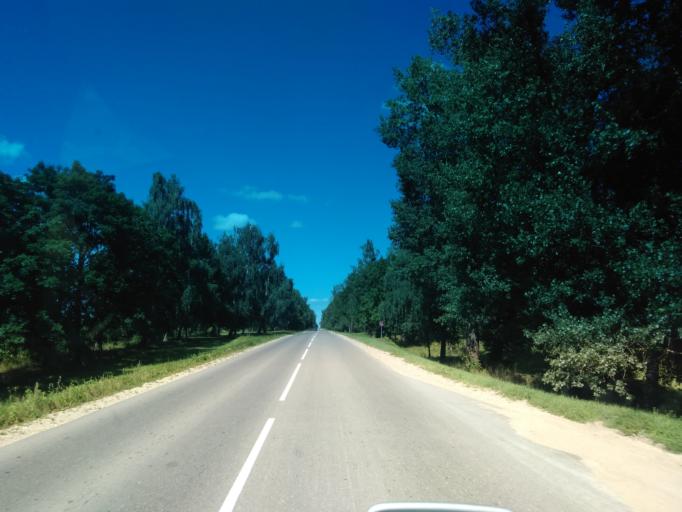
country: BY
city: Fanipol
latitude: 53.6987
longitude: 27.3549
